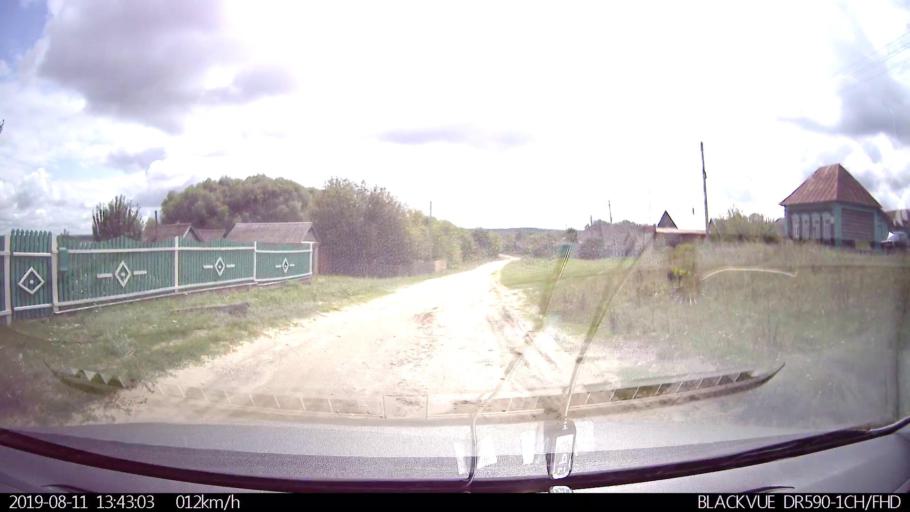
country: RU
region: Ulyanovsk
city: Ignatovka
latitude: 53.8555
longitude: 47.5749
